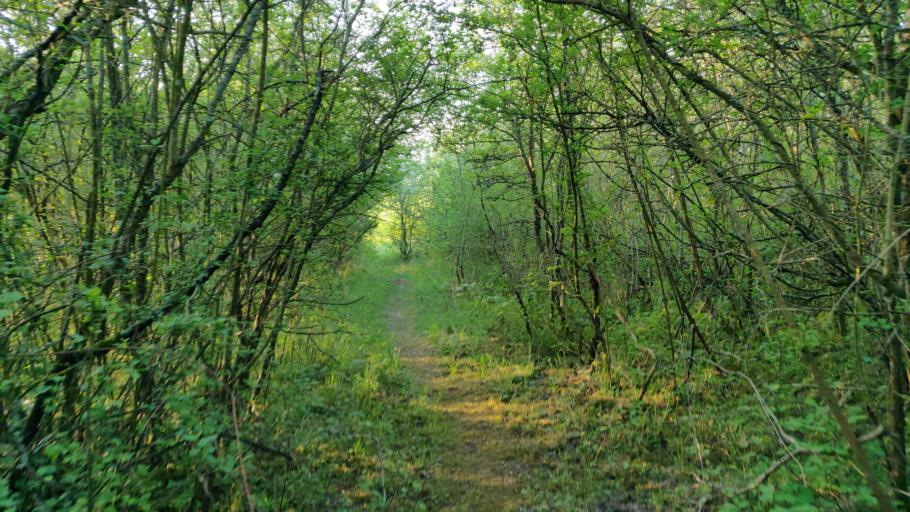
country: FR
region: Ile-de-France
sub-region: Departement des Yvelines
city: Freneuse
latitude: 49.0439
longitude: 1.6485
